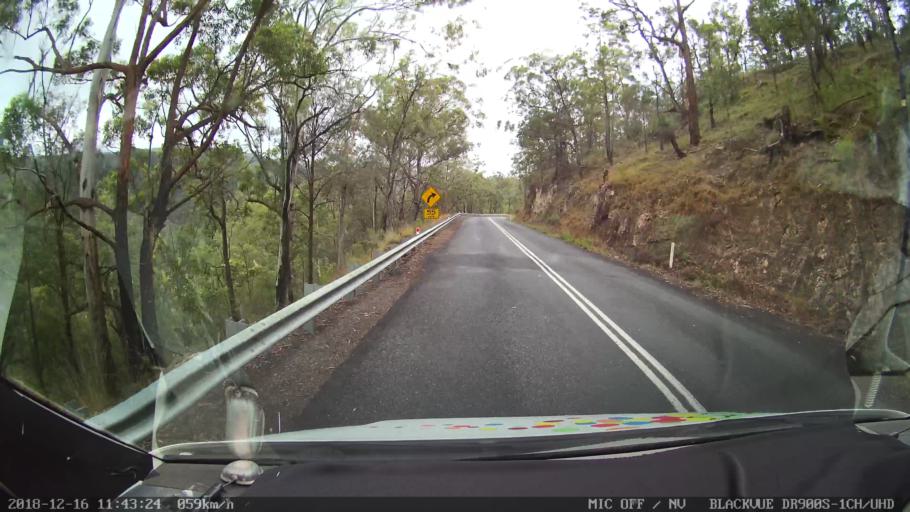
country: AU
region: New South Wales
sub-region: Tenterfield Municipality
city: Carrolls Creek
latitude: -28.9456
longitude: 152.2166
